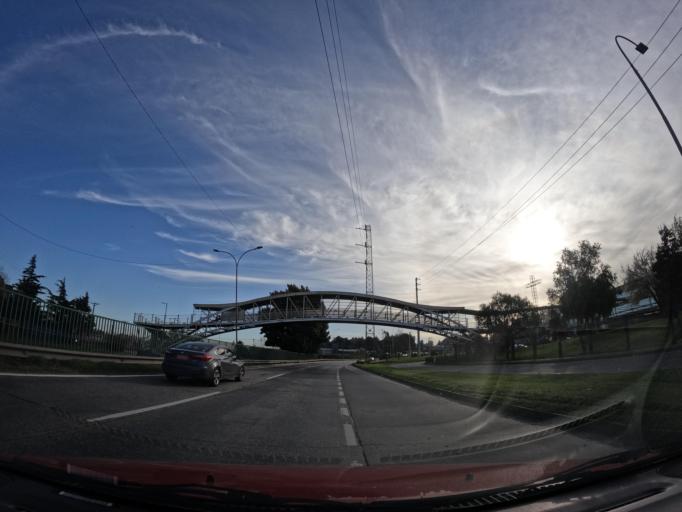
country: CL
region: Biobio
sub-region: Provincia de Concepcion
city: Concepcion
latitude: -36.7990
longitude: -73.0557
